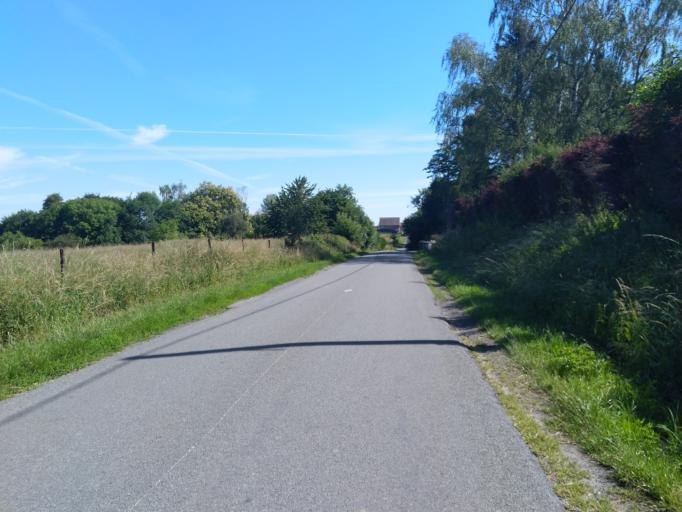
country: FR
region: Nord-Pas-de-Calais
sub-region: Departement du Nord
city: La Longueville
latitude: 50.3298
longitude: 3.8332
